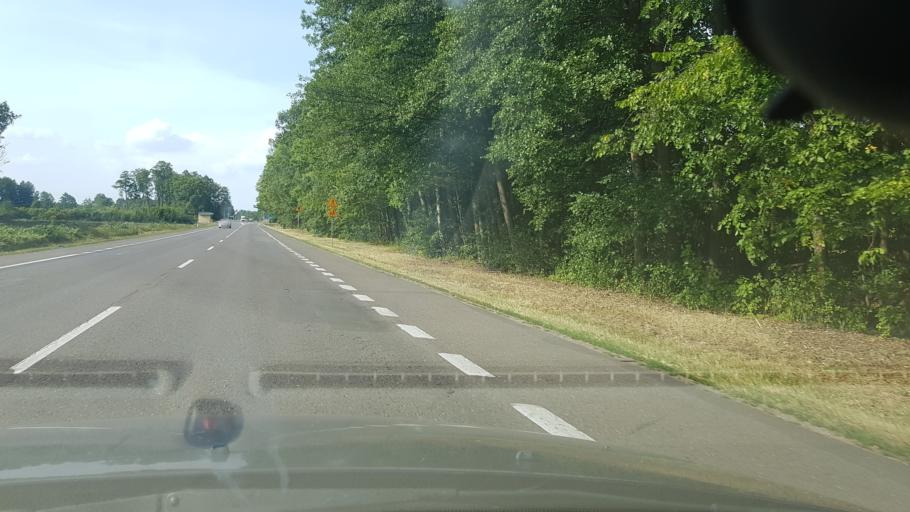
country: PL
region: Masovian Voivodeship
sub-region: Powiat ciechanowski
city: Glinojeck
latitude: 52.7487
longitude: 20.3152
